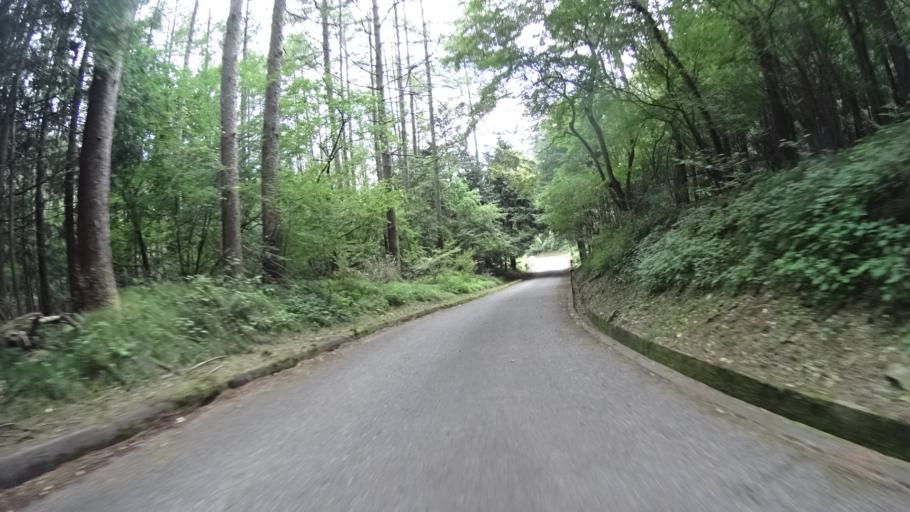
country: JP
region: Yamanashi
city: Nirasaki
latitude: 35.8019
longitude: 138.5266
